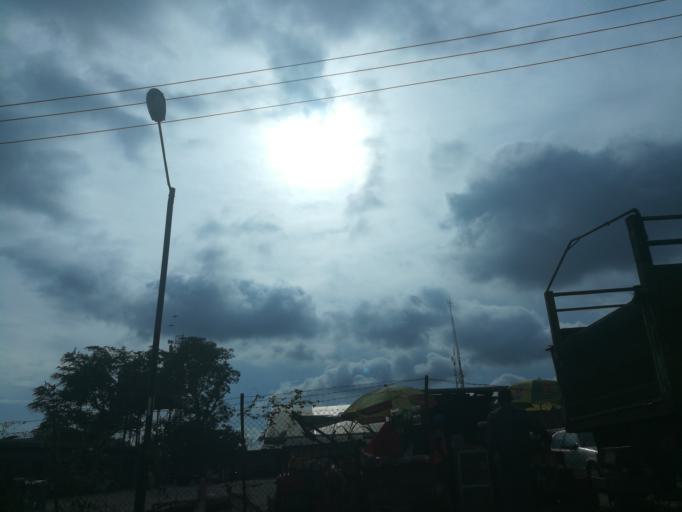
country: NG
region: Lagos
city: Ikeja
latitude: 6.6185
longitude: 3.3558
